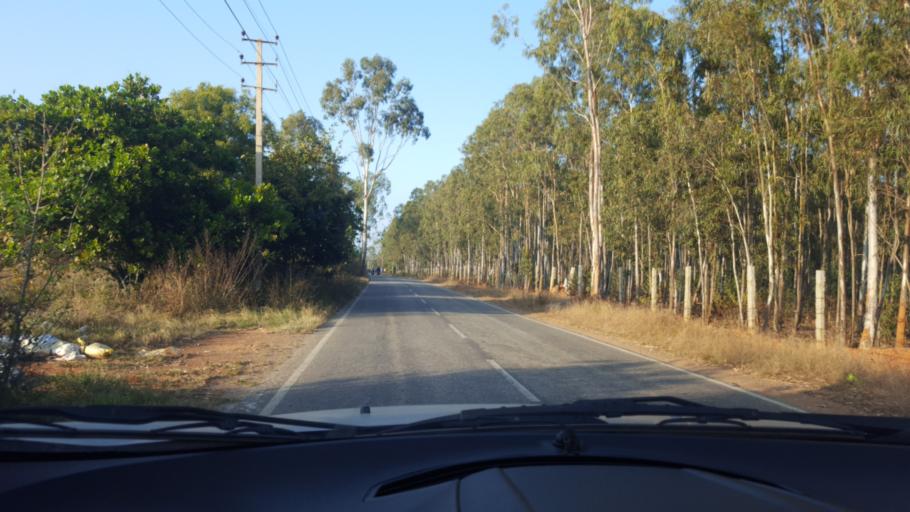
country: IN
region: Karnataka
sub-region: Bangalore Urban
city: Yelahanka
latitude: 13.1801
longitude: 77.5994
